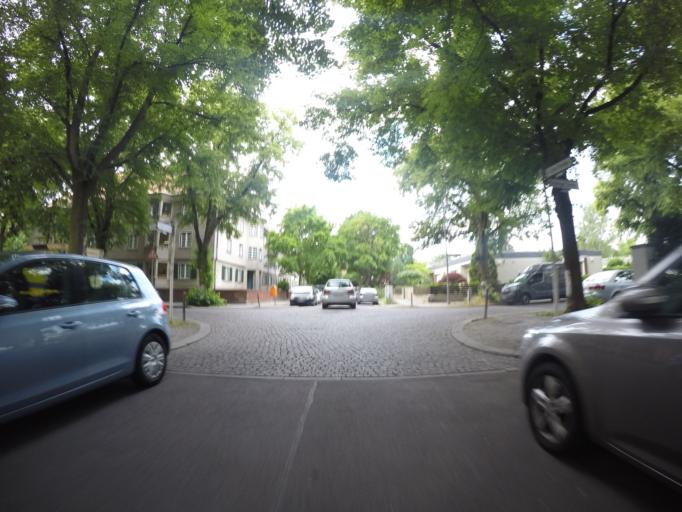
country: DE
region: Berlin
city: Schmargendorf
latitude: 52.4791
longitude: 13.2939
